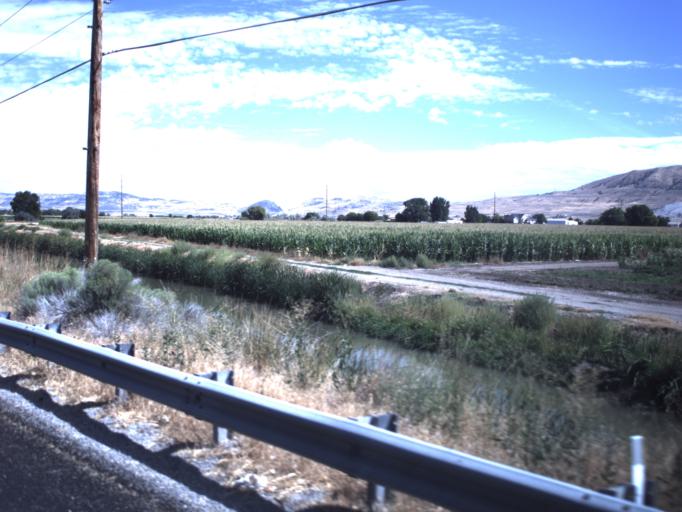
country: US
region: Utah
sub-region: Box Elder County
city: Tremonton
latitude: 41.7228
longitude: -112.1427
